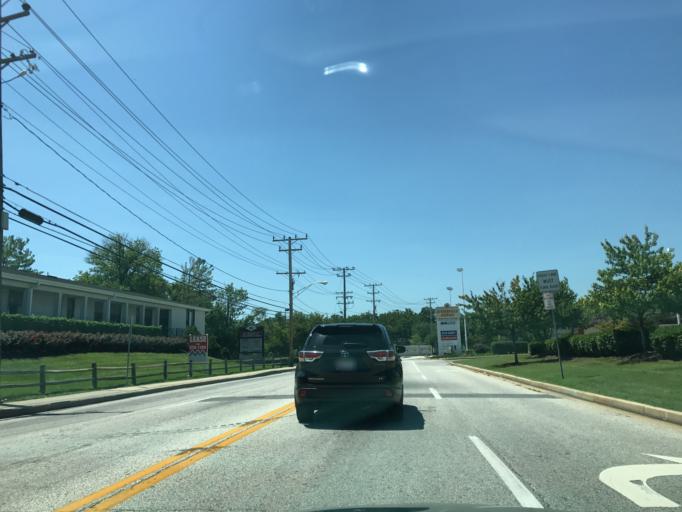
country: US
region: Maryland
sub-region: Baltimore County
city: Lutherville
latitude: 39.4292
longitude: -76.6240
